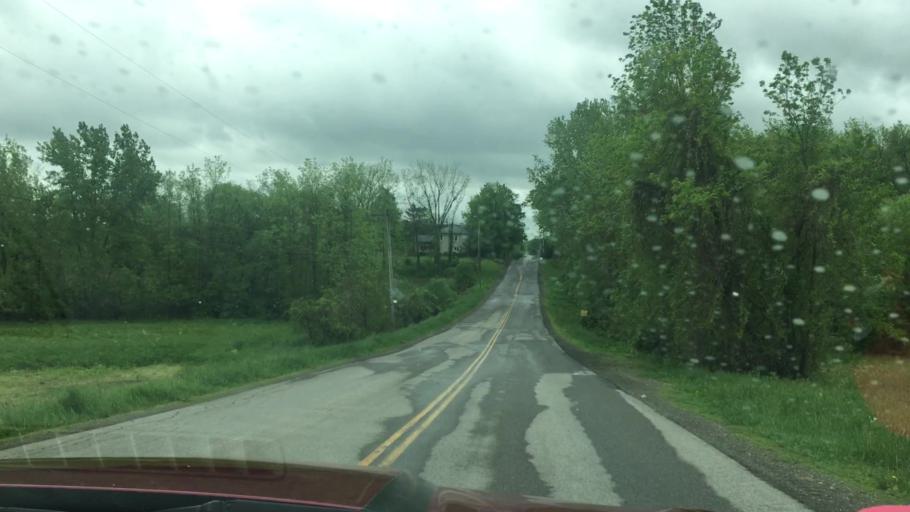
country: US
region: New York
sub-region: Genesee County
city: Batavia
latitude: 43.0828
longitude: -78.1395
